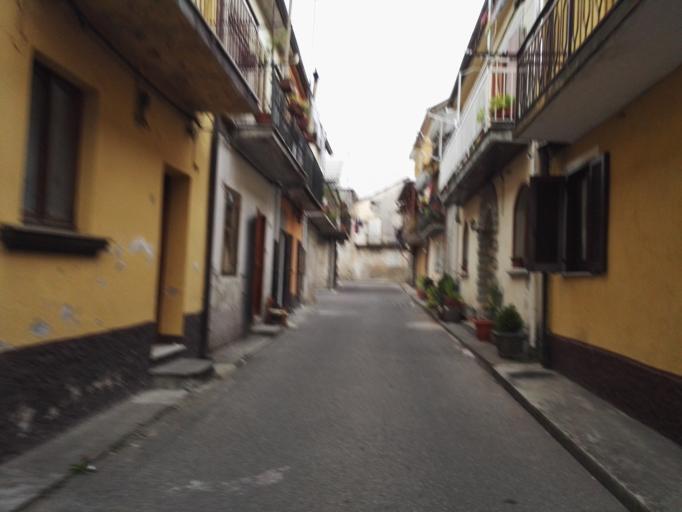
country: IT
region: Calabria
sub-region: Provincia di Vibo-Valentia
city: Serra San Bruno
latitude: 38.5732
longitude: 16.3276
